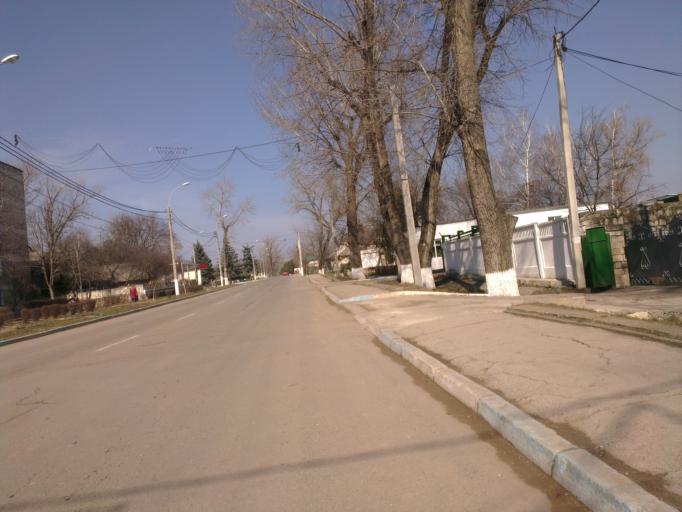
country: MD
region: Chisinau
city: Cricova
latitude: 47.1405
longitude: 28.8650
